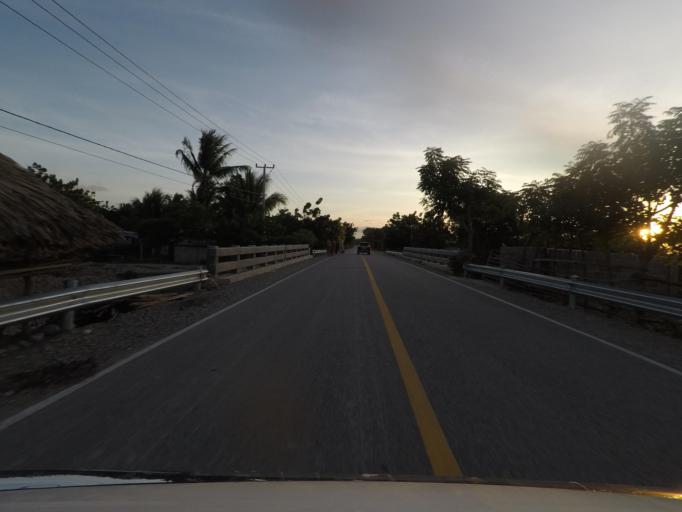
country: TL
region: Baucau
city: Baucau
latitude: -8.4307
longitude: 126.6817
